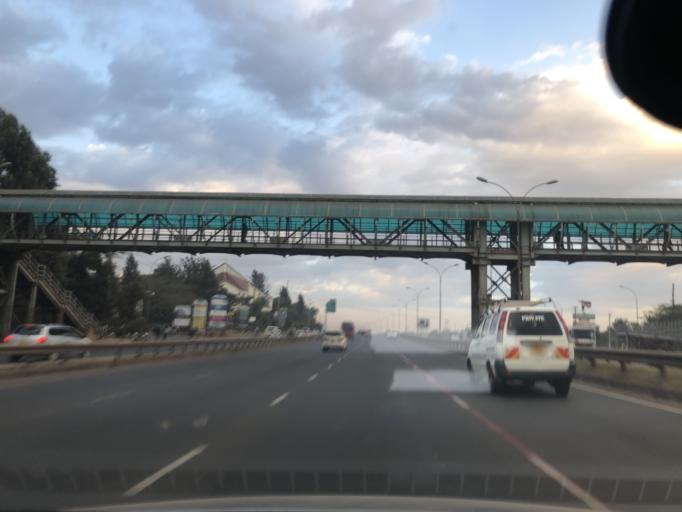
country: KE
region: Nairobi Area
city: Pumwani
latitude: -1.2259
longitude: 36.8845
